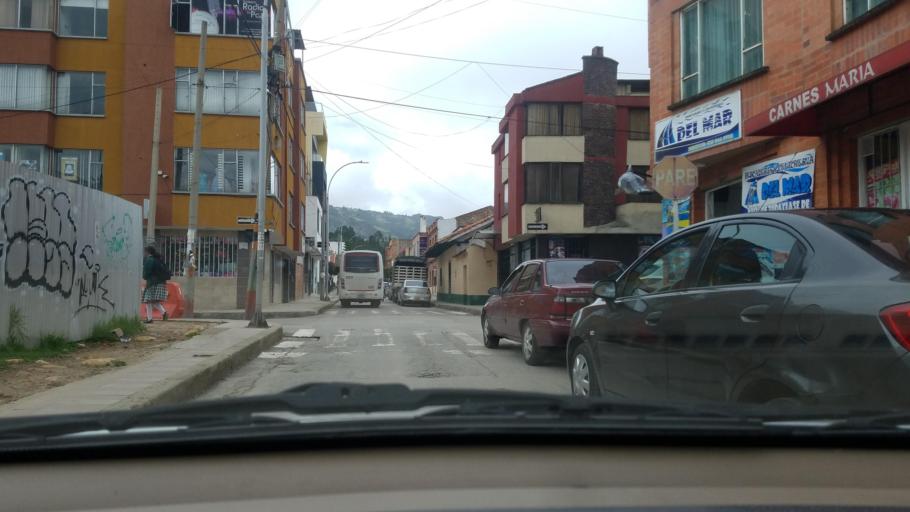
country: CO
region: Boyaca
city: Paipa
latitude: 5.7813
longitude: -73.1167
